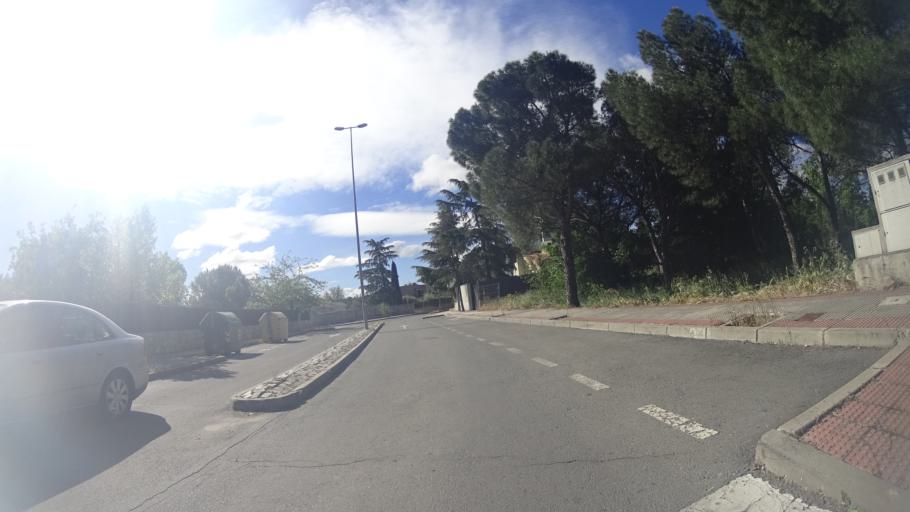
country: ES
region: Madrid
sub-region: Provincia de Madrid
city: Villanueva del Pardillo
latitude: 40.4890
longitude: -3.9400
